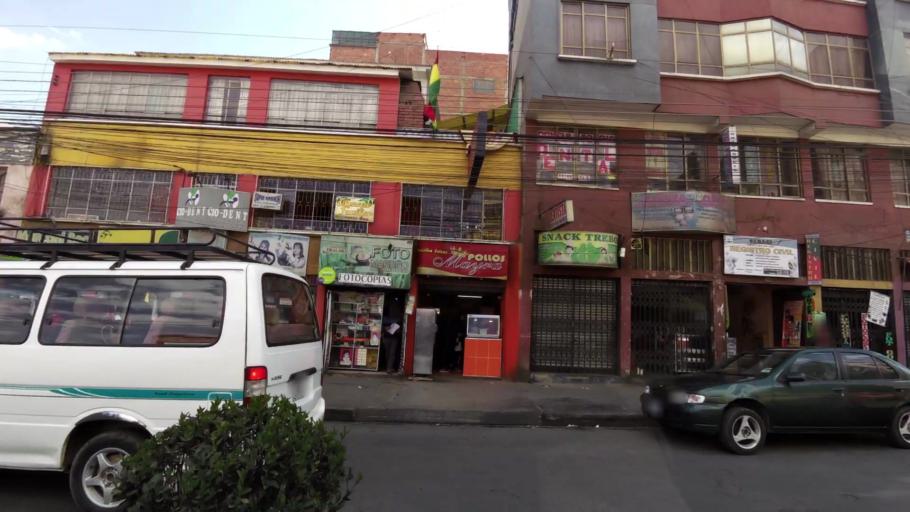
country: BO
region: La Paz
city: La Paz
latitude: -16.4818
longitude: -68.1219
